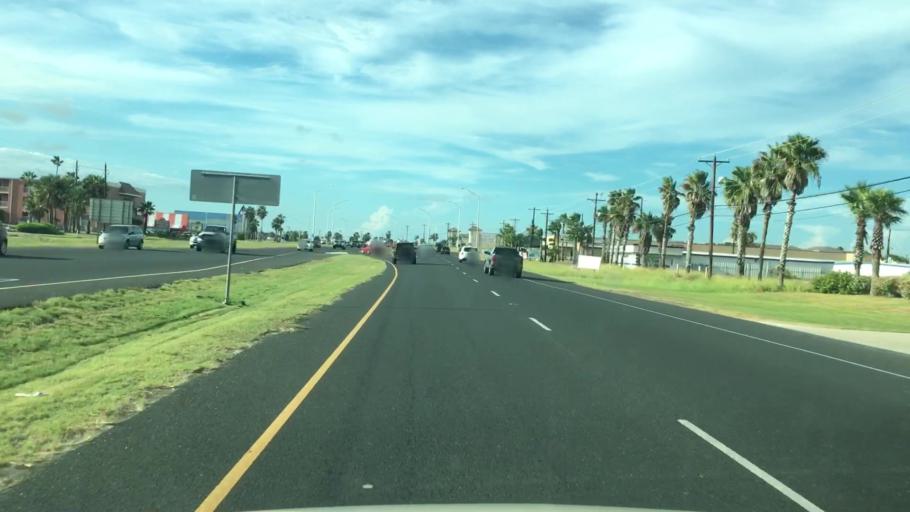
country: US
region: Texas
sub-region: Nueces County
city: Corpus Christi
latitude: 27.6209
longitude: -97.2216
